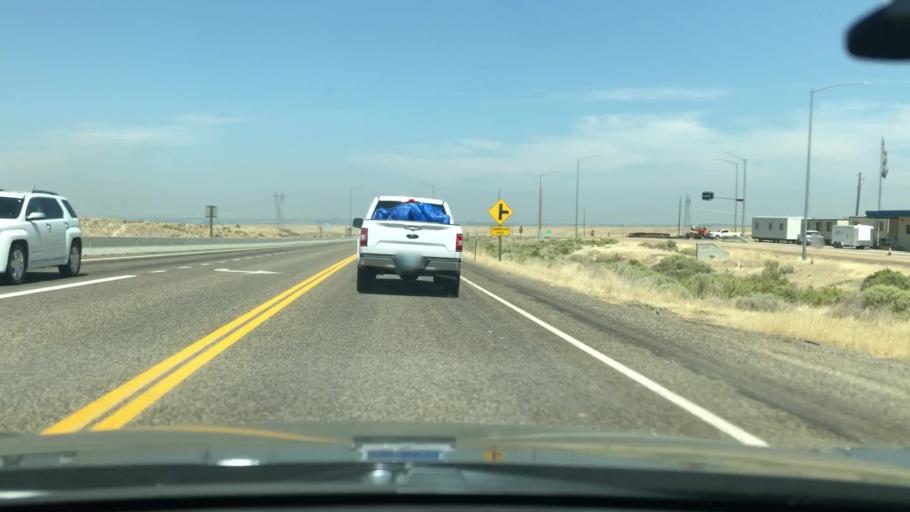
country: US
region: Idaho
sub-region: Owyhee County
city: Marsing
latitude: 43.4636
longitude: -116.8663
